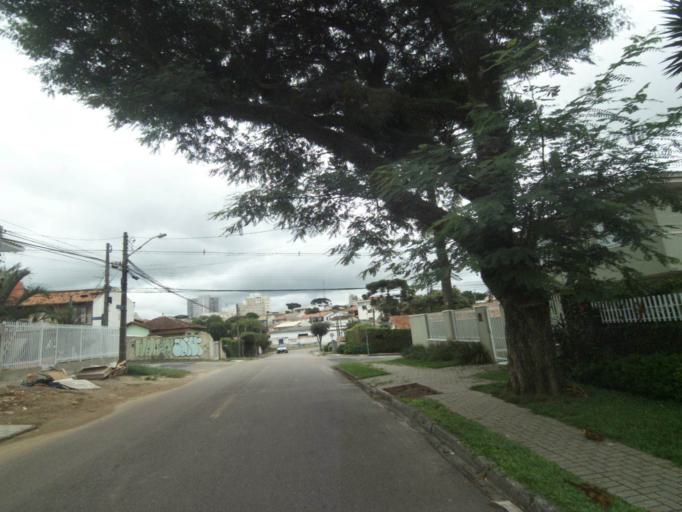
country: BR
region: Parana
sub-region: Curitiba
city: Curitiba
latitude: -25.4874
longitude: -49.2886
